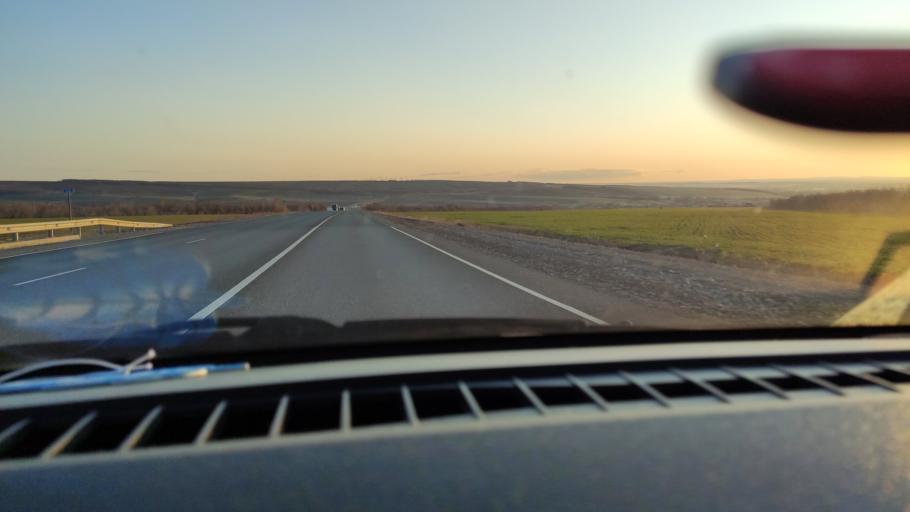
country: RU
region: Saratov
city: Sinodskoye
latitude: 51.9058
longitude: 46.5493
